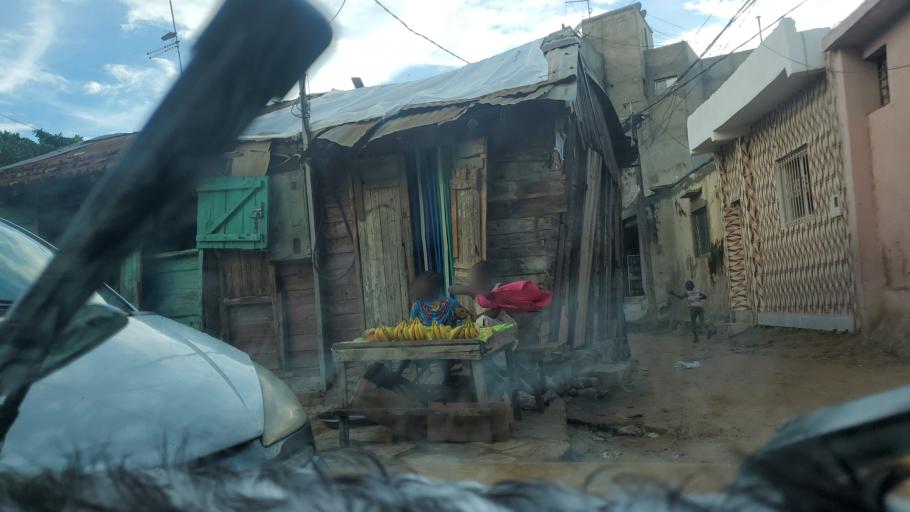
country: SN
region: Dakar
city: Mermoz Boabab
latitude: 14.7222
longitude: -17.4897
